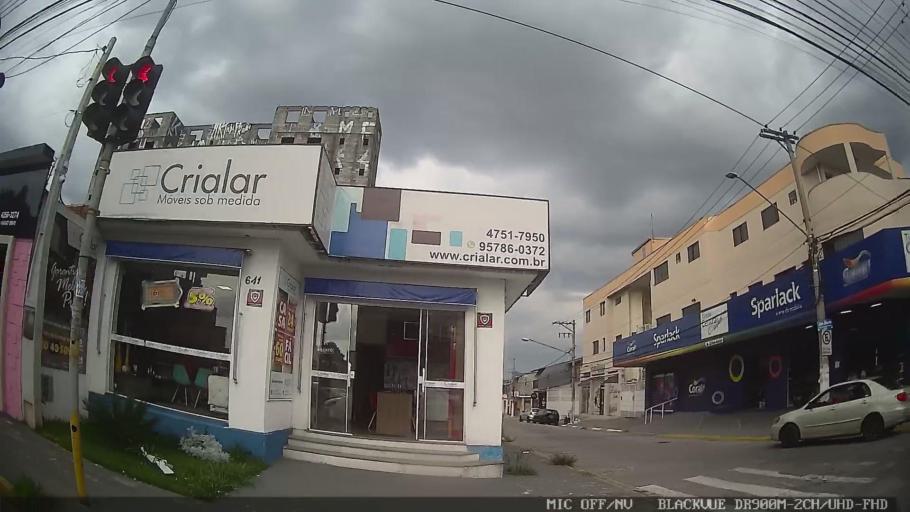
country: BR
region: Sao Paulo
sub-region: Suzano
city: Suzano
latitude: -23.5412
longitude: -46.3064
